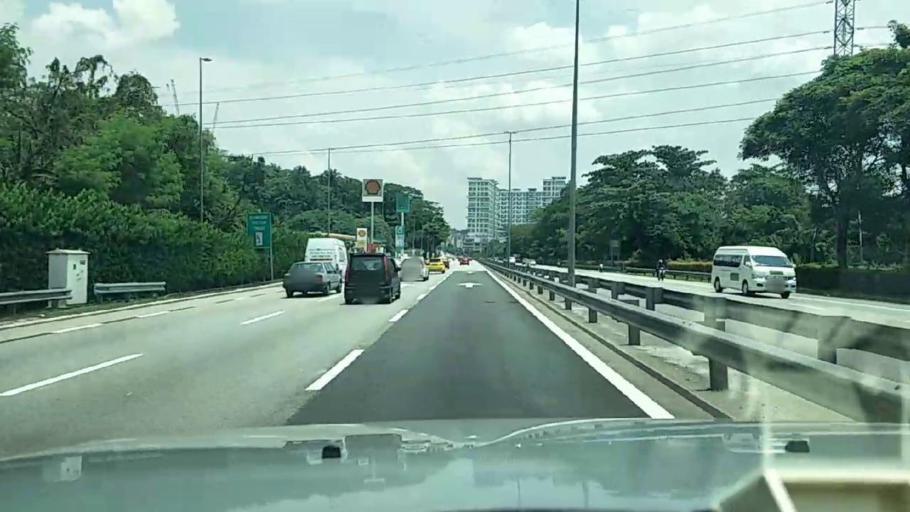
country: MY
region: Kuala Lumpur
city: Kuala Lumpur
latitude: 3.0941
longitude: 101.6826
